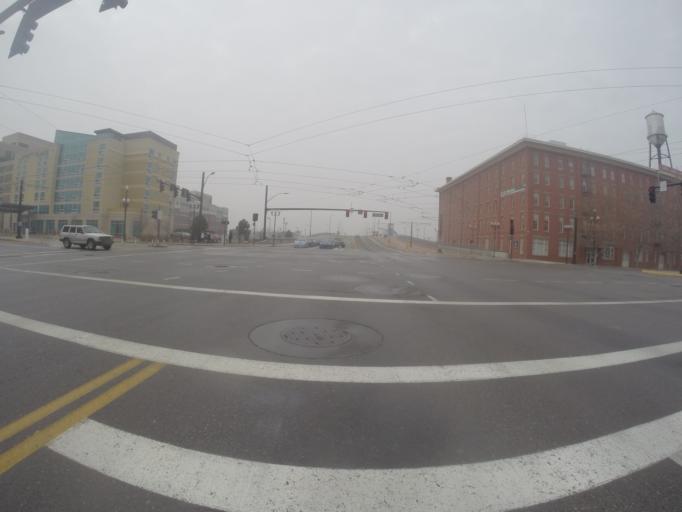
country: US
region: Utah
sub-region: Salt Lake County
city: Salt Lake City
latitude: 40.7715
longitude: -111.9023
